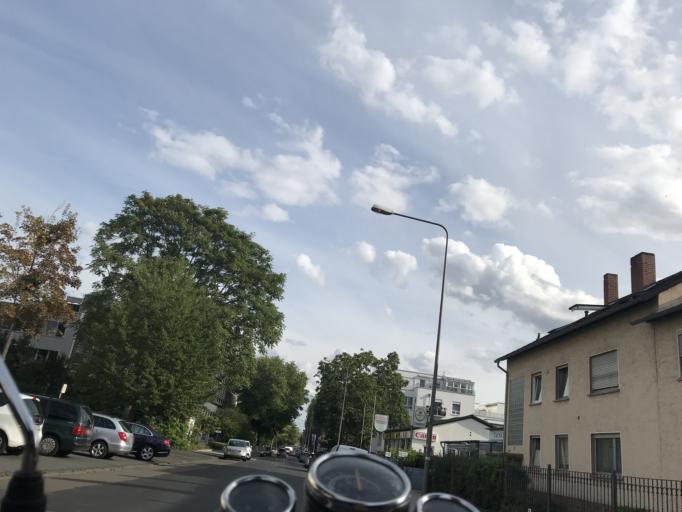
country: DE
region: Hesse
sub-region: Regierungsbezirk Darmstadt
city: Wiesbaden
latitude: 50.0672
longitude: 8.2548
